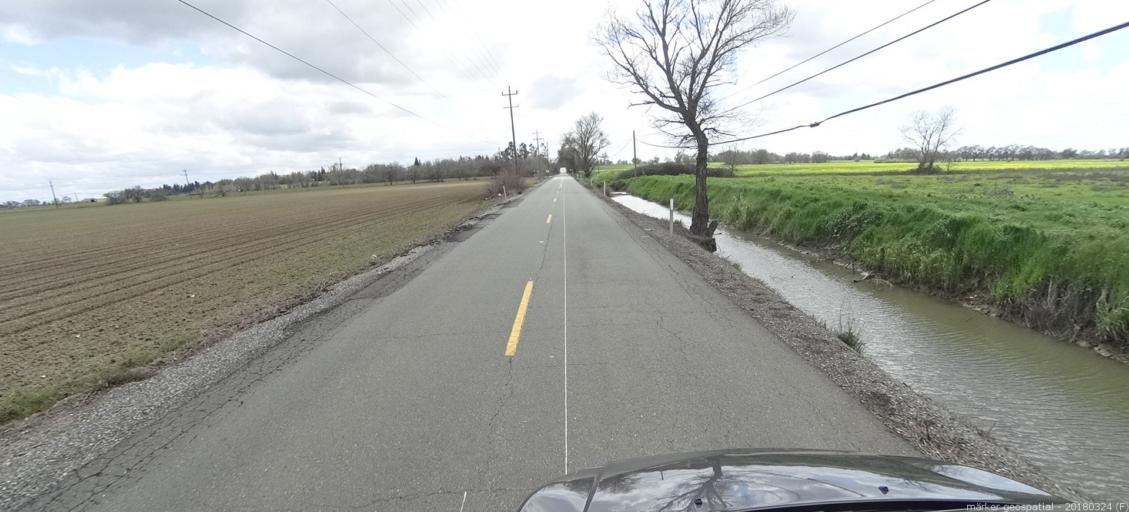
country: US
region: California
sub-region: Yolo County
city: West Sacramento
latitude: 38.6586
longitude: -121.5767
